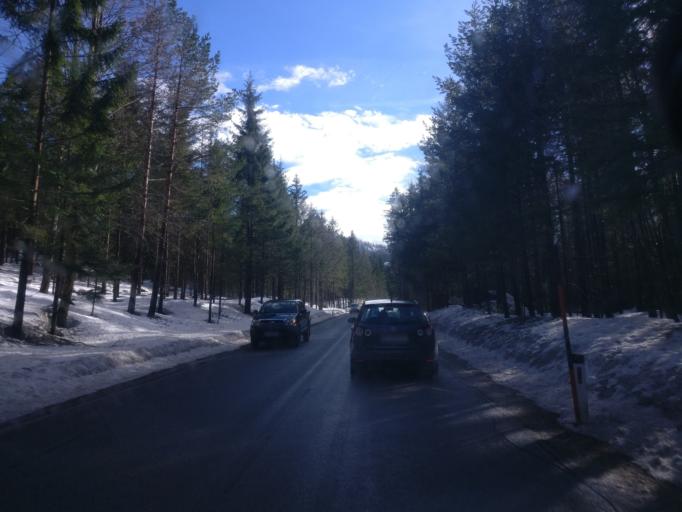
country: AT
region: Styria
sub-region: Politischer Bezirk Liezen
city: Sankt Gallen
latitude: 47.6283
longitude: 14.5577
